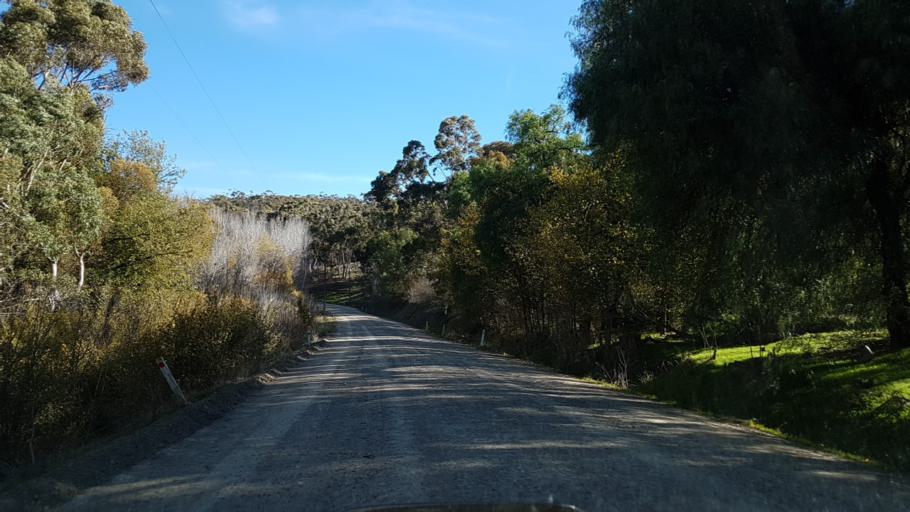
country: AU
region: South Australia
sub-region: Northern Areas
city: Jamestown
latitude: -33.2777
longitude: 138.5693
